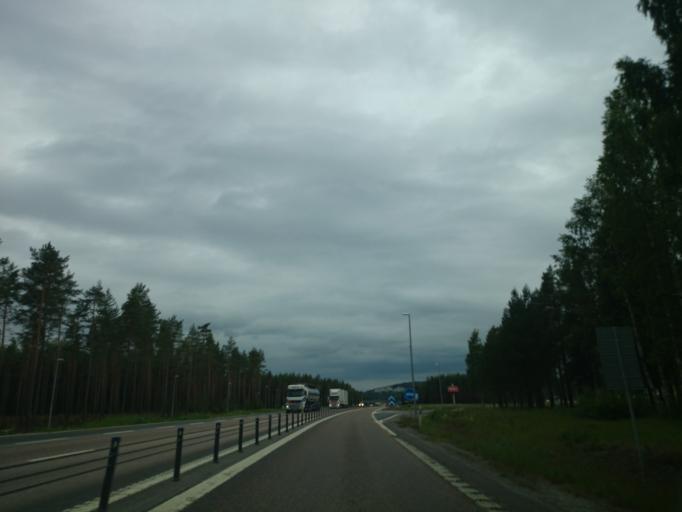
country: SE
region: Vaesternorrland
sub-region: Timra Kommun
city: Bergeforsen
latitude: 62.5062
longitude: 17.3562
